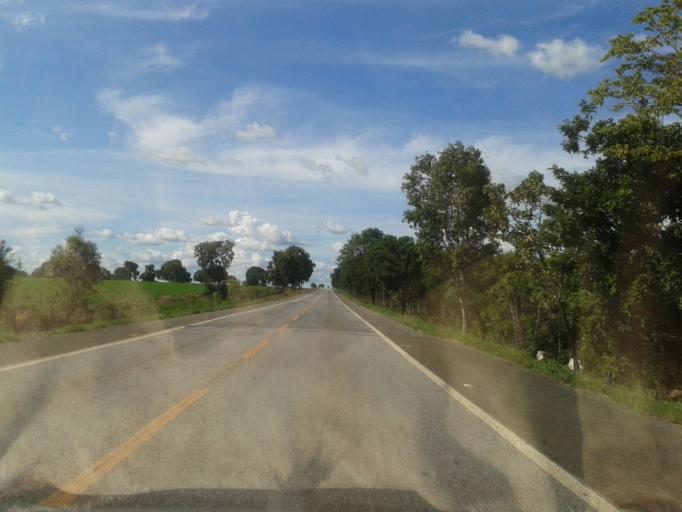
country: BR
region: Goias
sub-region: Mozarlandia
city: Mozarlandia
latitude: -14.8928
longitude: -50.5497
